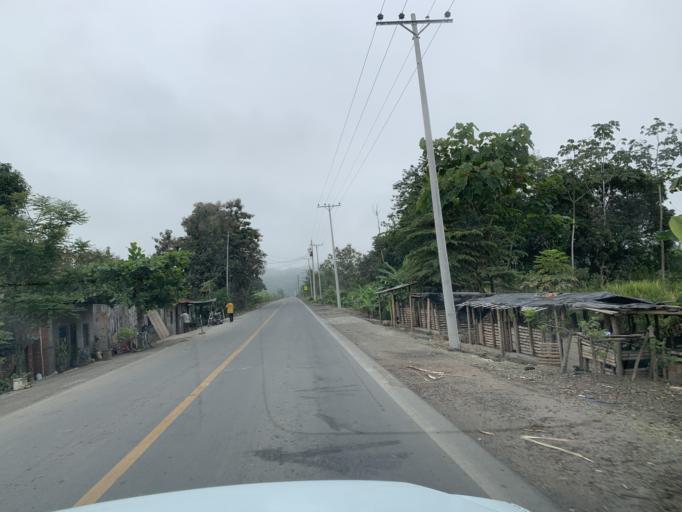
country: EC
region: Guayas
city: Coronel Marcelino Mariduena
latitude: -2.3399
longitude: -79.5293
